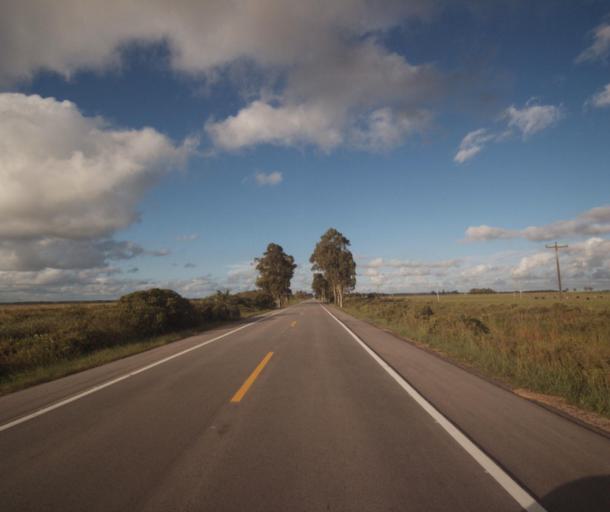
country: BR
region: Rio Grande do Sul
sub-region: Rio Grande
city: Rio Grande
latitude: -32.1382
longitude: -52.3781
